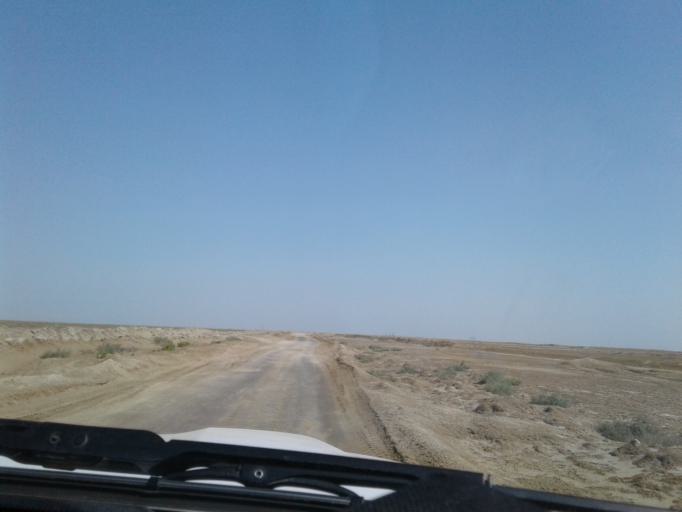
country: IR
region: Golestan
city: Gomishan
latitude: 37.8290
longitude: 53.9215
